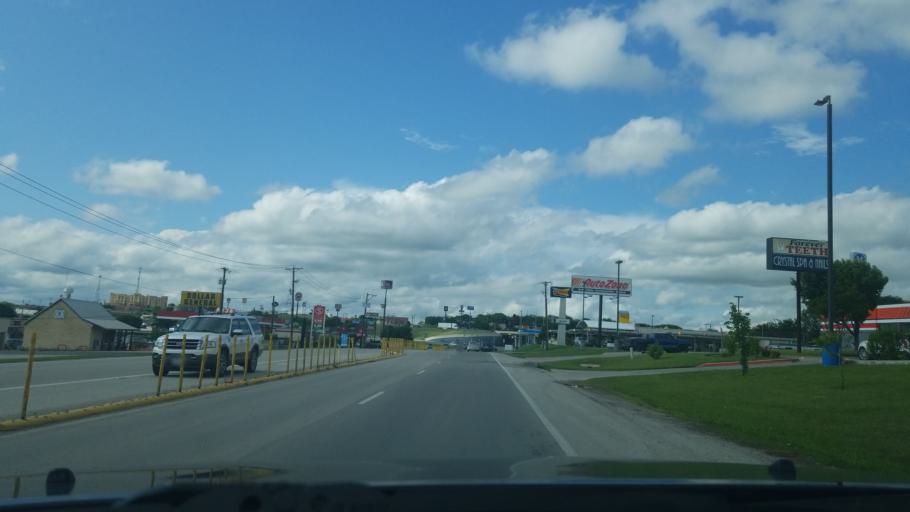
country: US
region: Texas
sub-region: Wise County
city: Decatur
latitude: 33.2236
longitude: -97.5939
